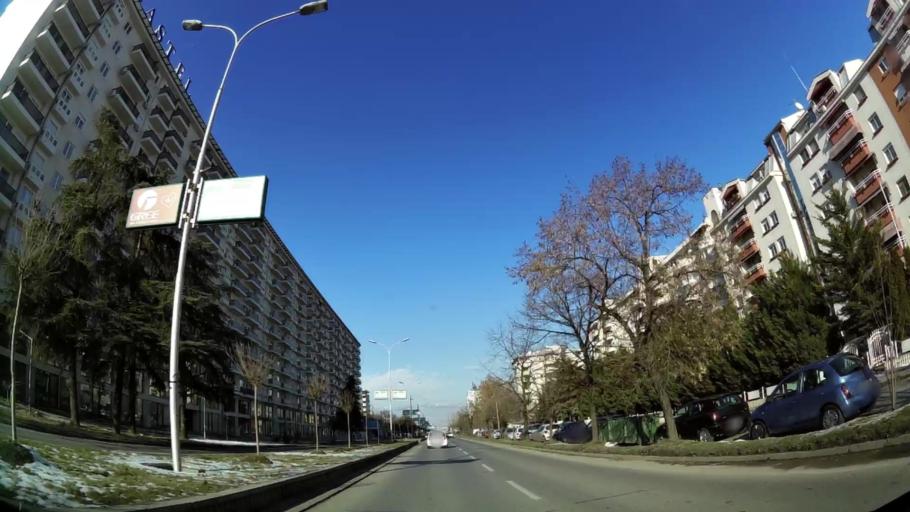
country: MK
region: Karpos
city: Skopje
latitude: 41.9983
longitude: 21.4040
